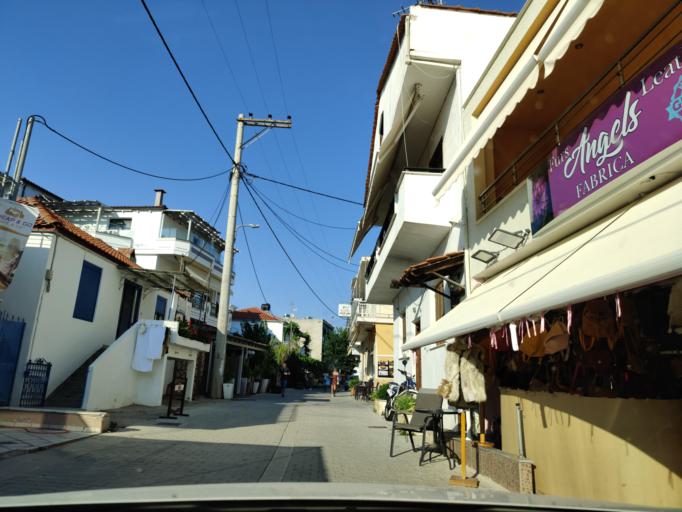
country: GR
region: East Macedonia and Thrace
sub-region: Nomos Kavalas
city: Limenaria
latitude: 40.6107
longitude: 24.6060
